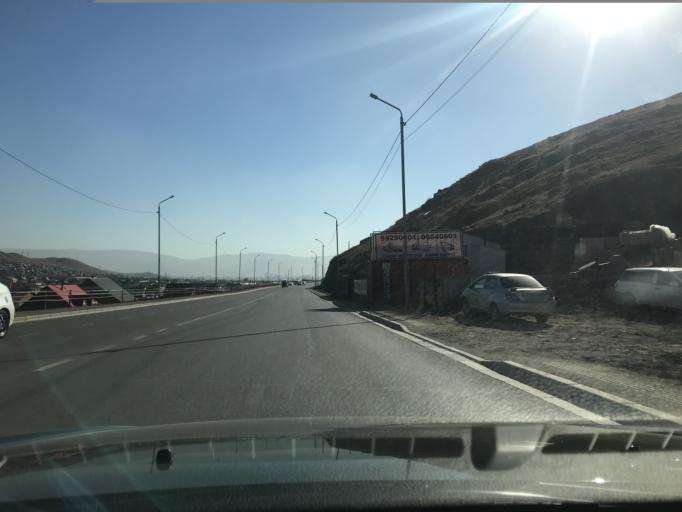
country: MN
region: Ulaanbaatar
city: Ulaanbaatar
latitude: 47.9879
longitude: 106.9251
